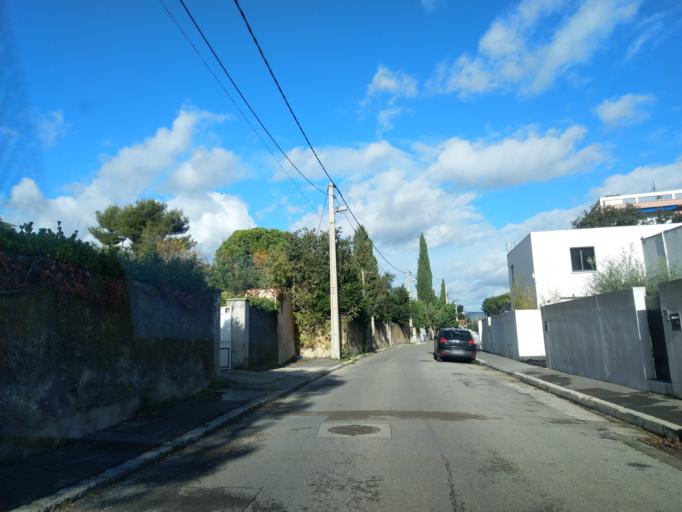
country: FR
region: Provence-Alpes-Cote d'Azur
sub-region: Departement des Bouches-du-Rhone
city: Marseille 12
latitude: 43.3100
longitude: 5.4353
